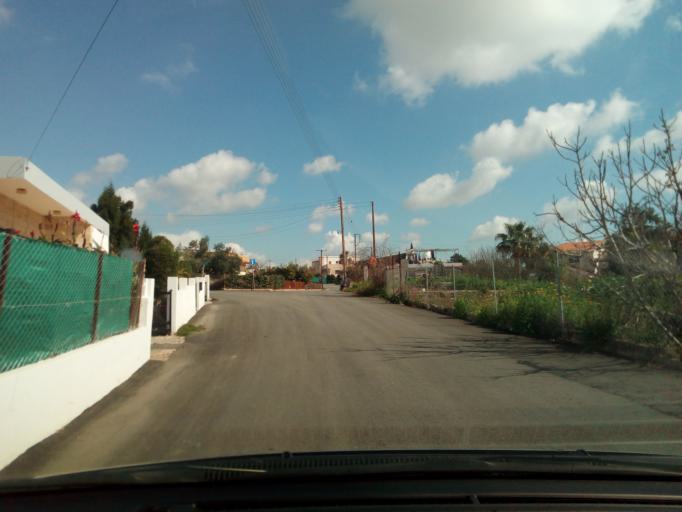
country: CY
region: Pafos
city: Empa
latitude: 34.8069
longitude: 32.4280
